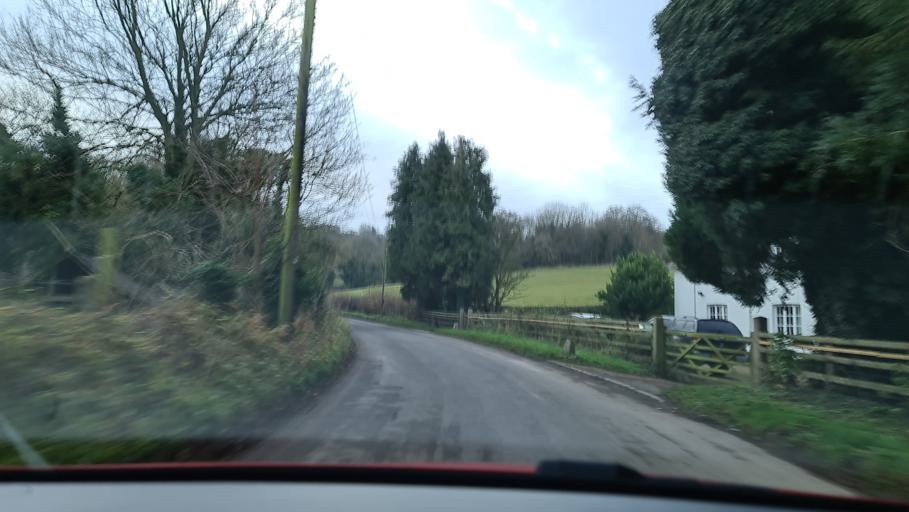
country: GB
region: England
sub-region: Buckinghamshire
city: Princes Risborough
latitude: 51.7154
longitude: -0.8140
